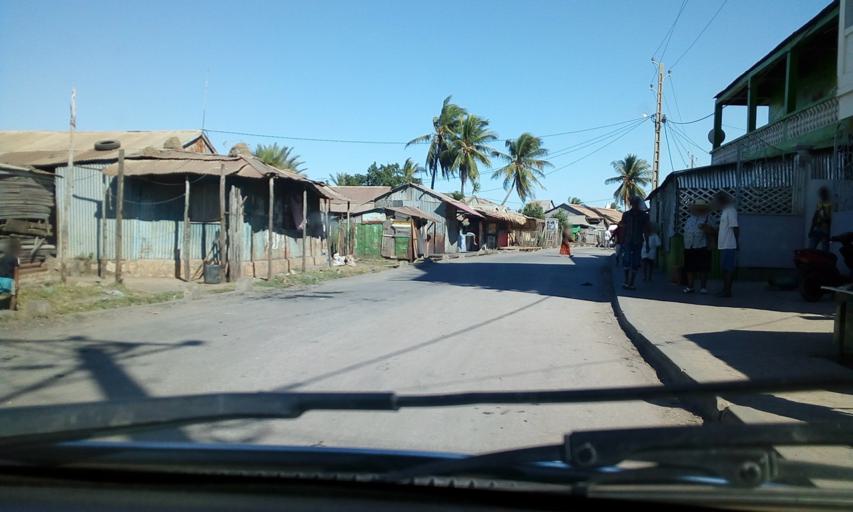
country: MG
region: Boeny
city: Mahajanga
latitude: -15.7096
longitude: 46.3286
